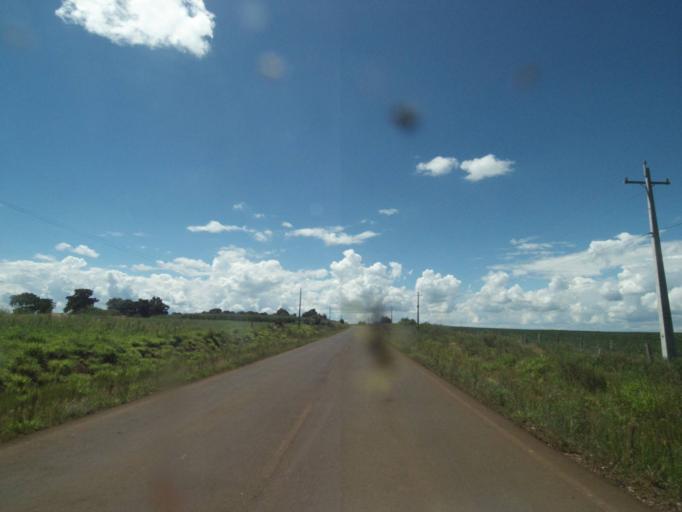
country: BR
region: Parana
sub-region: Pinhao
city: Pinhao
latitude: -25.8176
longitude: -52.0423
